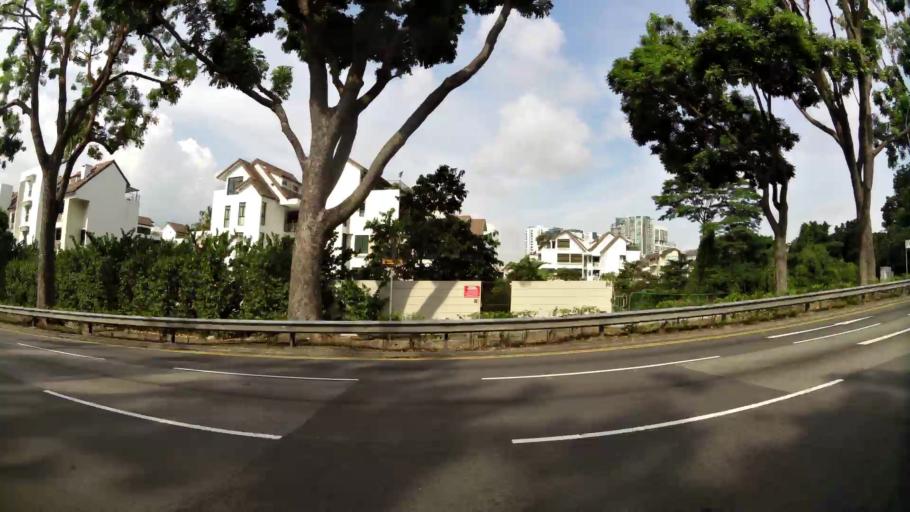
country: SG
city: Singapore
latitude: 1.2958
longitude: 103.7696
